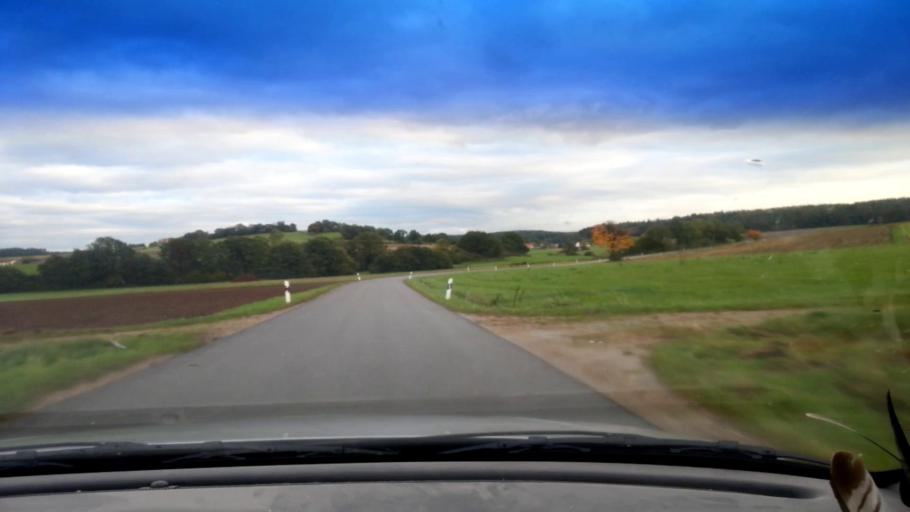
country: DE
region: Bavaria
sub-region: Upper Franconia
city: Burgebrach
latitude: 49.8149
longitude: 10.6879
